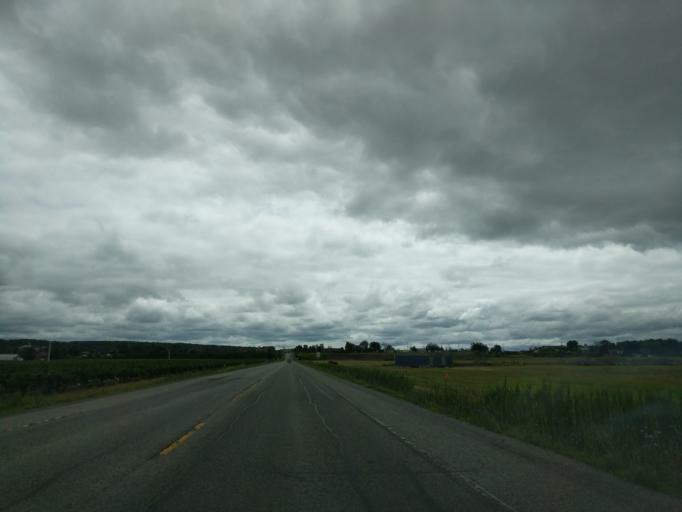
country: CA
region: Ontario
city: Thorold
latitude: 43.1698
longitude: -79.1686
